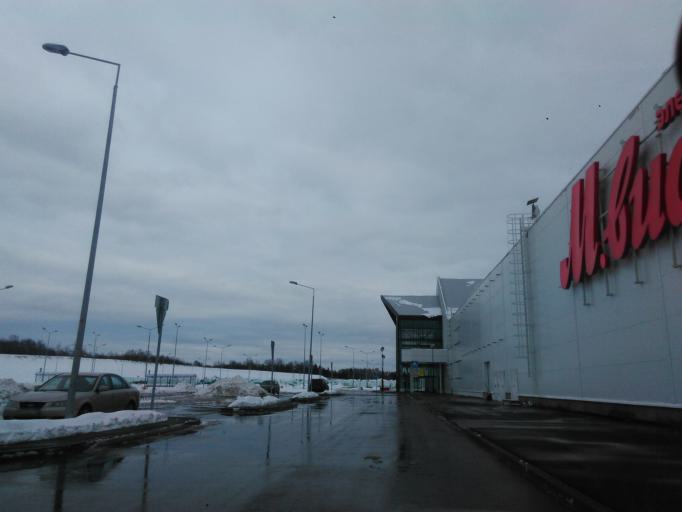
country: RU
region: Moskovskaya
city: Rzhavki
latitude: 56.0004
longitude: 37.2585
